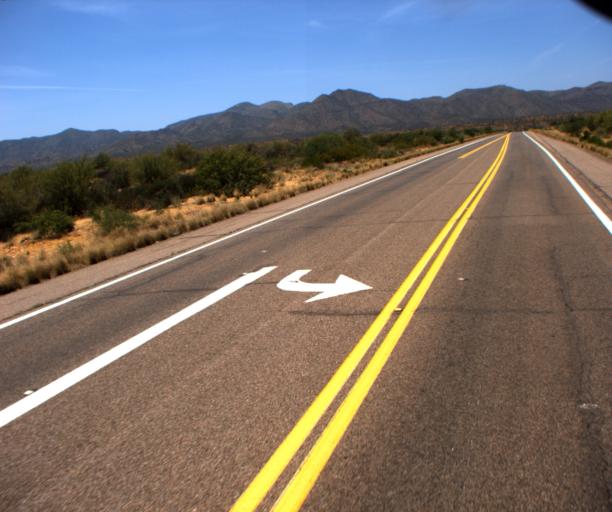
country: US
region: Arizona
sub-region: Gila County
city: Miami
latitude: 33.6165
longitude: -111.0425
